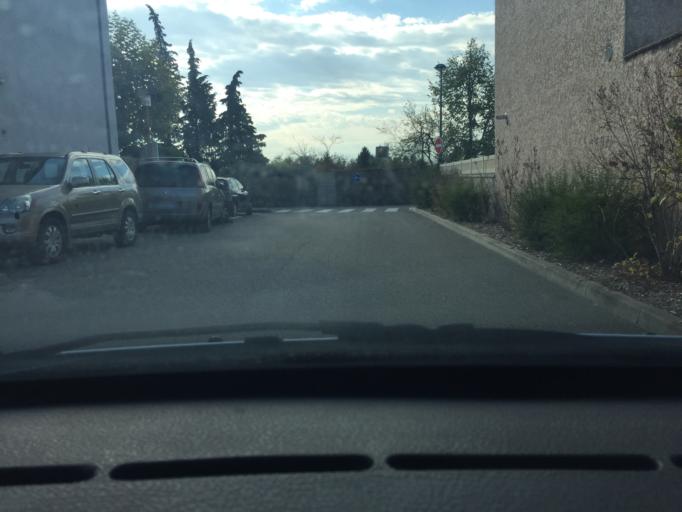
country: FR
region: Rhone-Alpes
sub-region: Departement de l'Ain
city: Miribel
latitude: 45.8237
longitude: 4.9579
